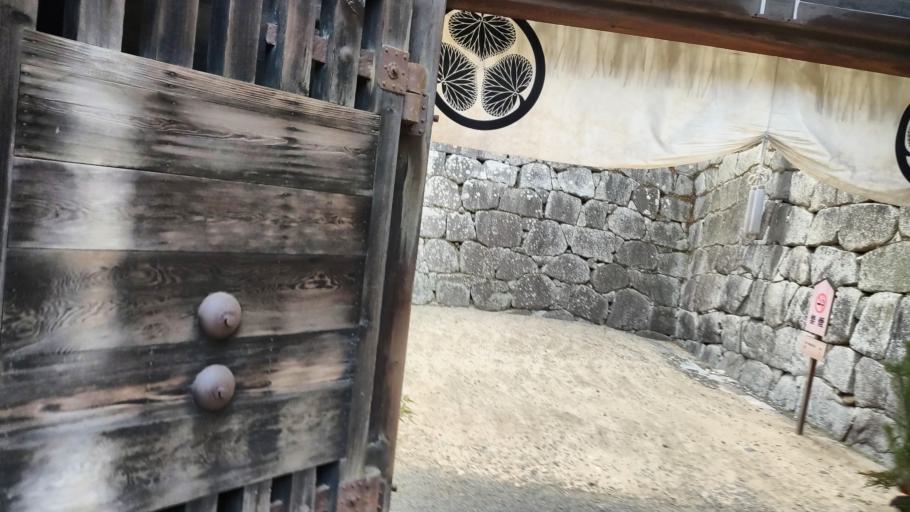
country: JP
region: Ehime
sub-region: Shikoku-chuo Shi
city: Matsuyama
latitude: 33.8454
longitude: 132.7659
